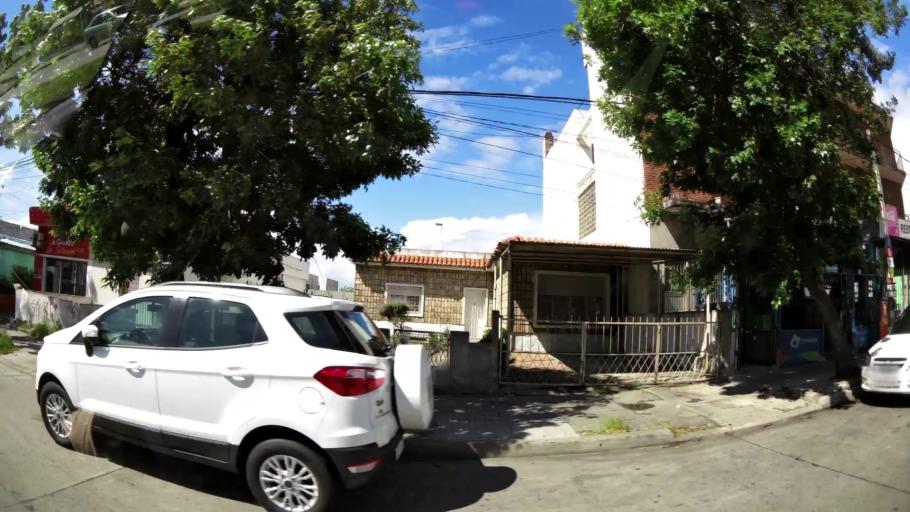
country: UY
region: Montevideo
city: Montevideo
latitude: -34.8499
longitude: -56.1856
